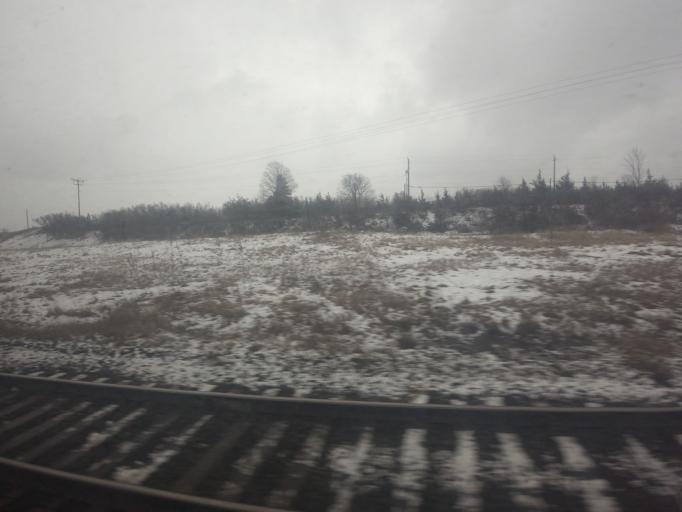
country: CA
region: Ontario
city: Quinte West
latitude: 44.0842
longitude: -77.6400
